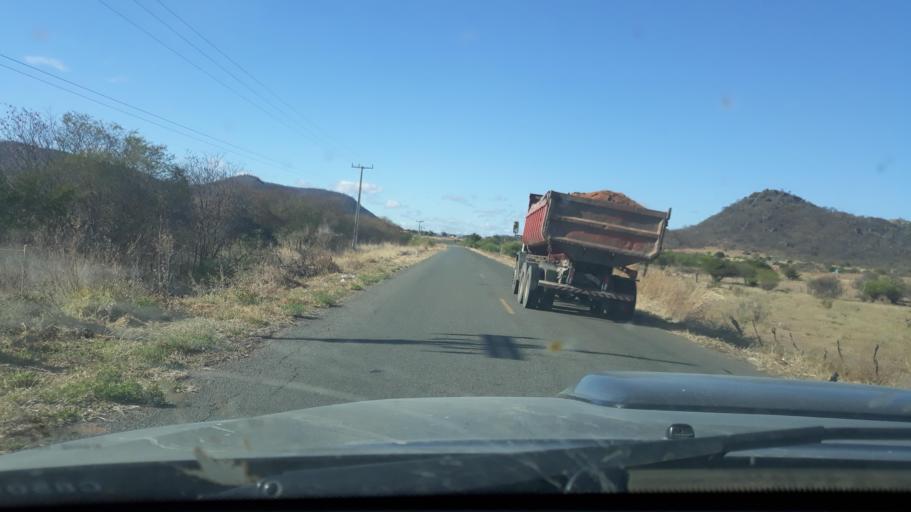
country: BR
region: Bahia
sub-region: Guanambi
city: Guanambi
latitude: -14.1072
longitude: -42.8664
